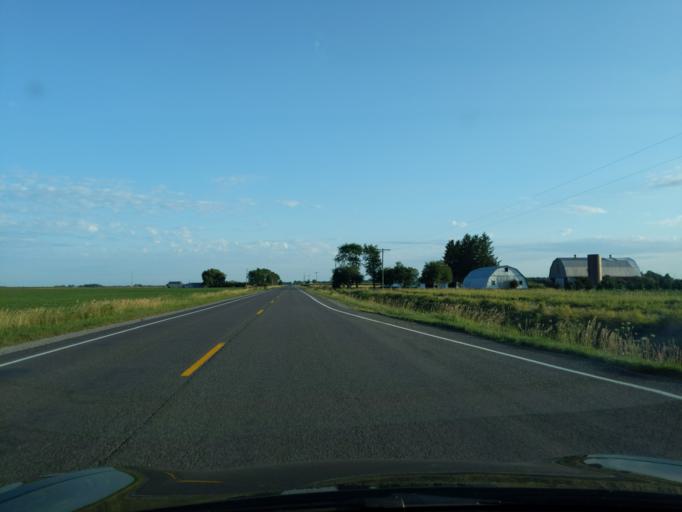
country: US
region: Michigan
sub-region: Gratiot County
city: Breckenridge
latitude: 43.4952
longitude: -84.3697
